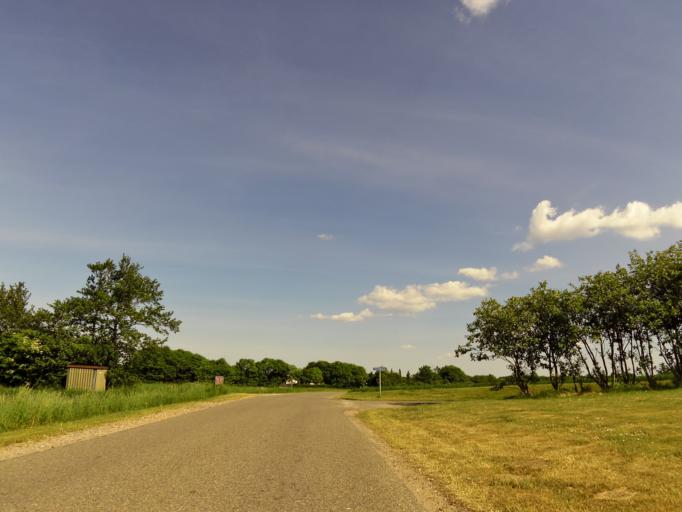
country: DK
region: Central Jutland
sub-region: Holstebro Kommune
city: Vinderup
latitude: 56.4336
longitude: 8.8869
